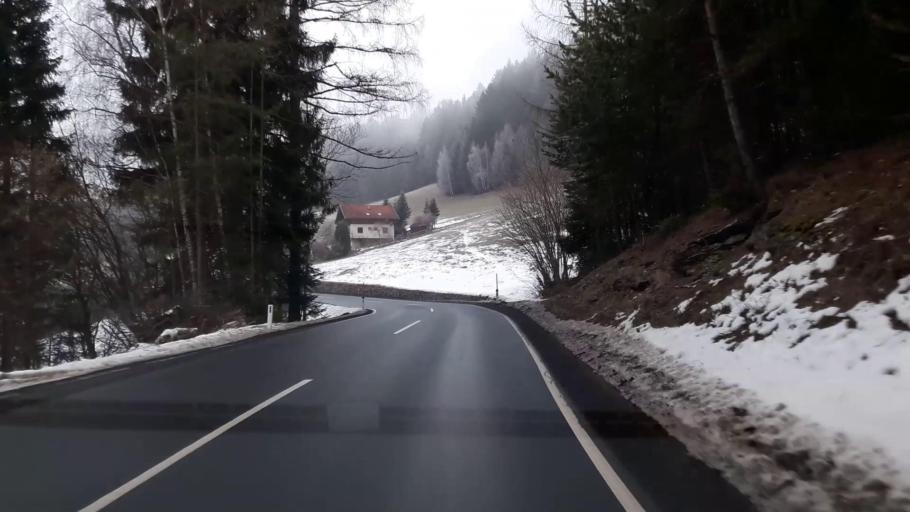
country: AT
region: Lower Austria
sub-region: Politischer Bezirk Neunkirchen
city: Feistritz am Wechsel
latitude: 47.5687
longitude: 16.0429
